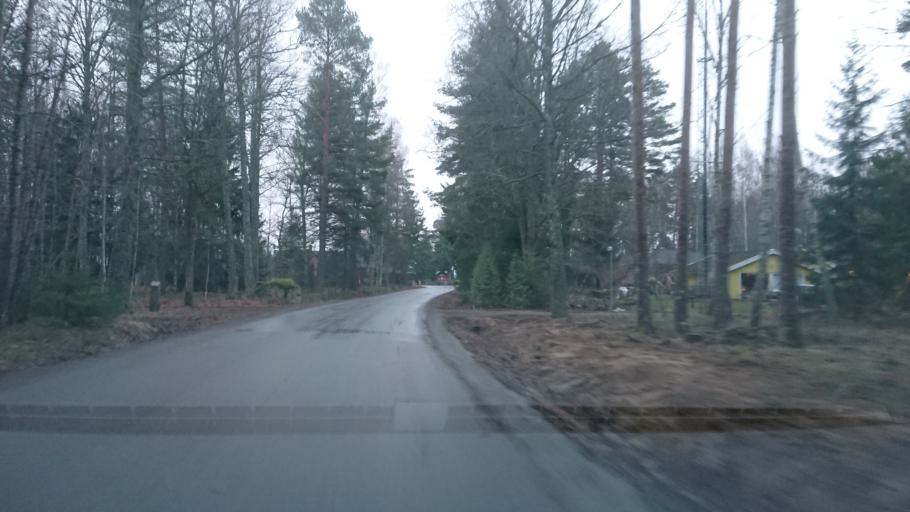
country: SE
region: Uppsala
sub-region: Osthammars Kommun
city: Bjorklinge
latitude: 59.9784
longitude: 17.5956
